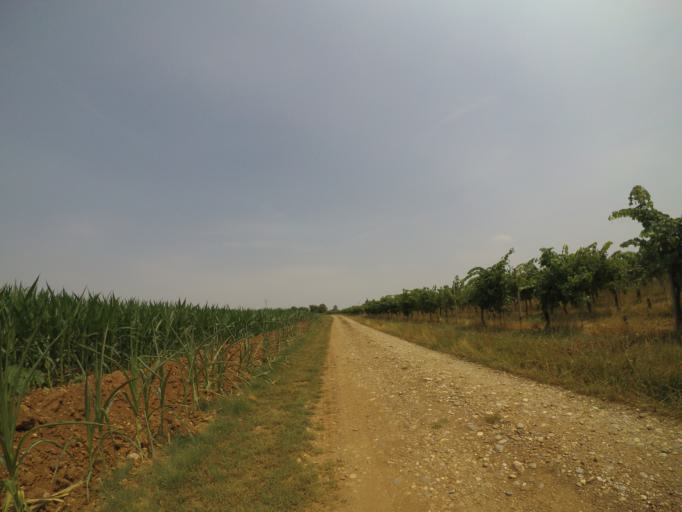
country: IT
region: Friuli Venezia Giulia
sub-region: Provincia di Udine
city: Bertiolo
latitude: 45.9535
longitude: 13.0494
